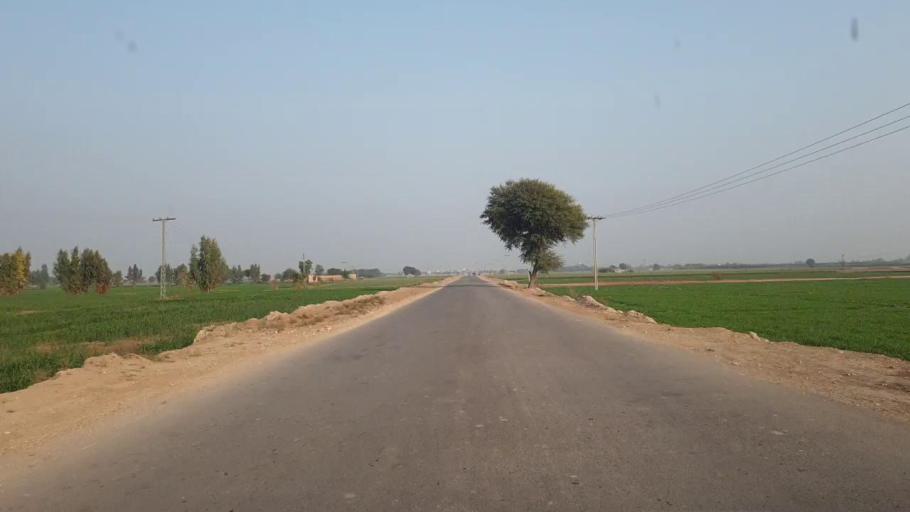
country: PK
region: Sindh
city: Bhit Shah
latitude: 25.8085
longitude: 68.4678
